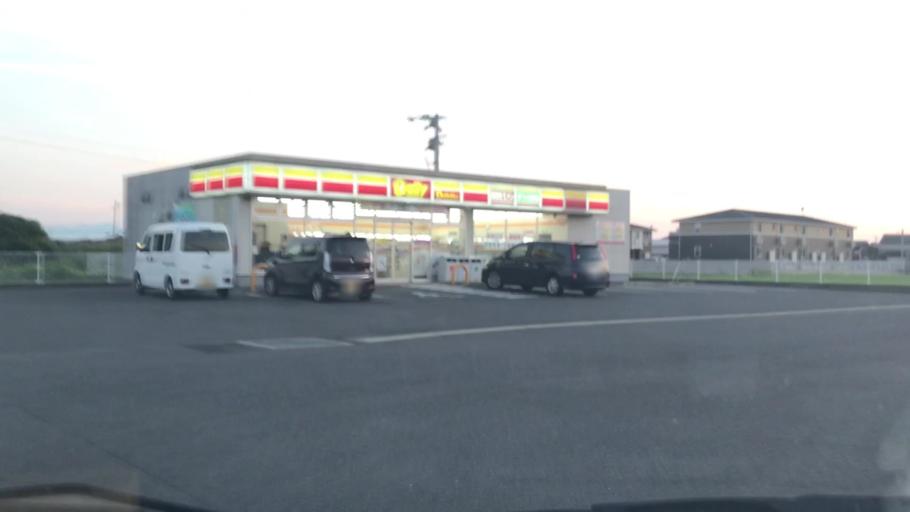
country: JP
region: Saga Prefecture
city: Saga-shi
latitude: 33.2206
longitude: 130.2091
